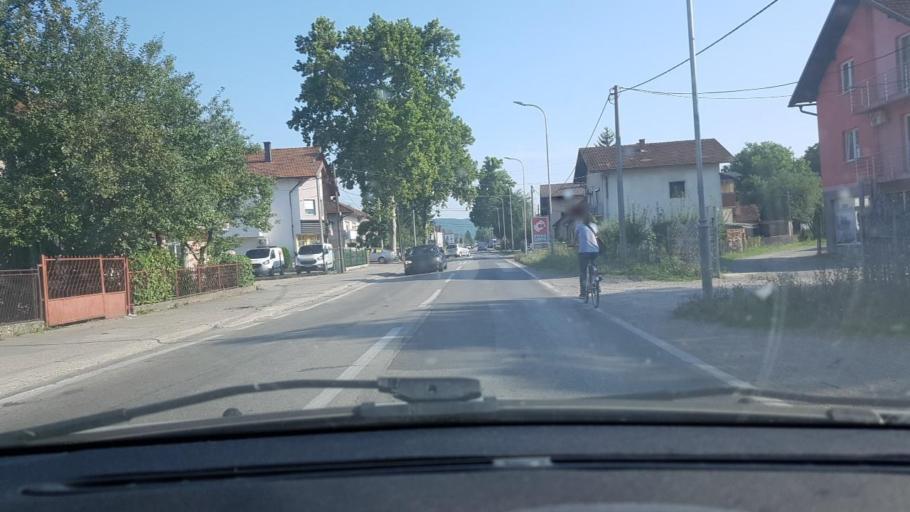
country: BA
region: Federation of Bosnia and Herzegovina
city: Bihac
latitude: 44.8222
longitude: 15.8817
